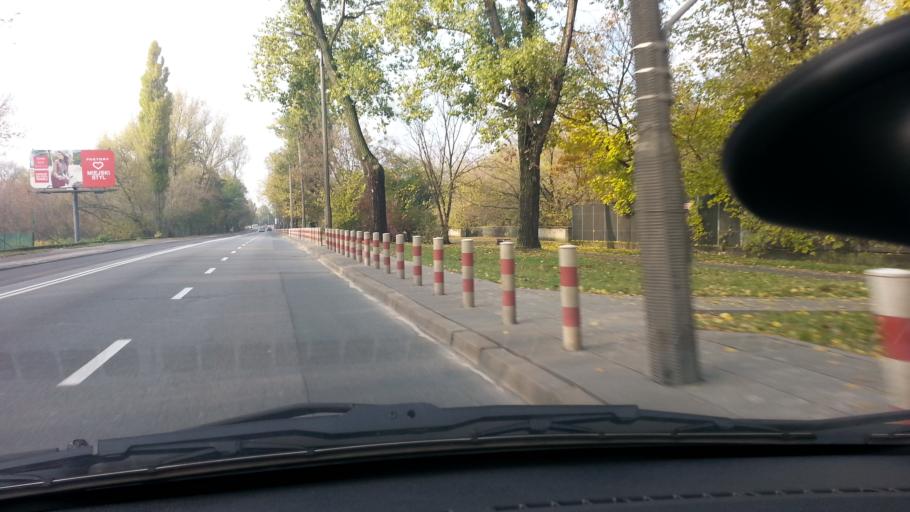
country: PL
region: Masovian Voivodeship
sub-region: Warszawa
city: Praga Polnoc
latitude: 52.2576
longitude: 21.0188
